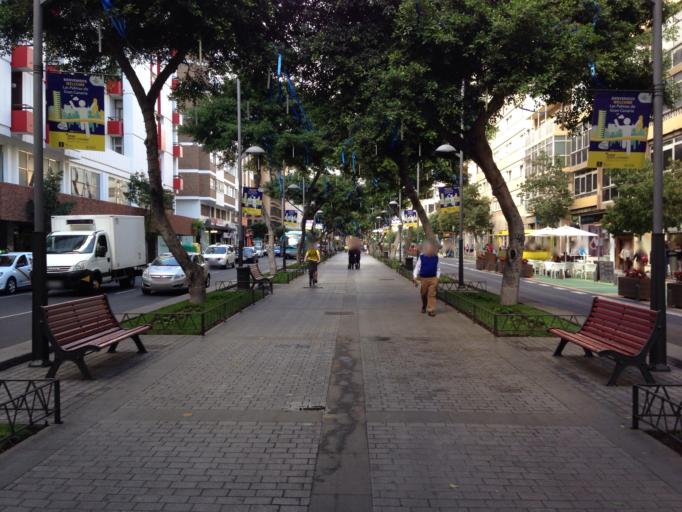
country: ES
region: Canary Islands
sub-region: Provincia de Las Palmas
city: Las Palmas de Gran Canaria
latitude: 28.1349
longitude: -15.4321
